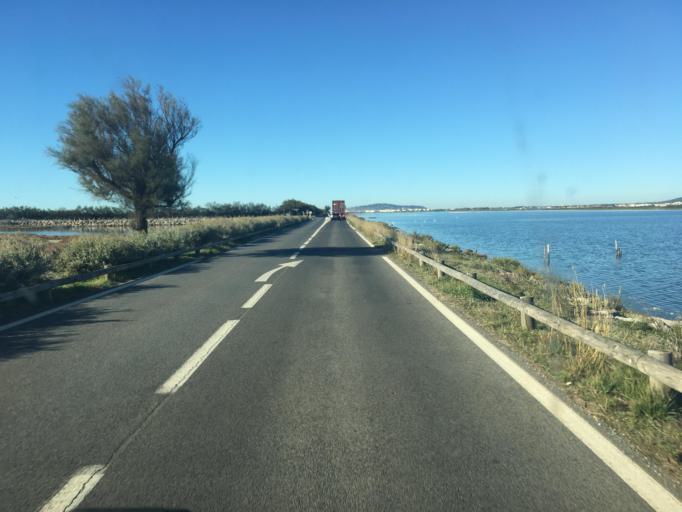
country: FR
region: Languedoc-Roussillon
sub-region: Departement de l'Herault
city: Vic-la-Gardiole
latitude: 43.4565
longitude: 3.8131
